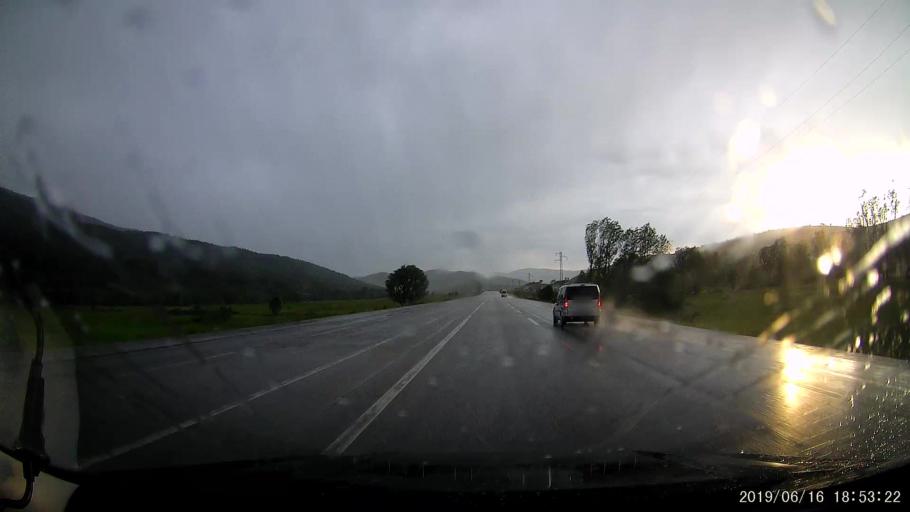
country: TR
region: Erzincan
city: Catalcam
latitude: 39.8987
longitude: 38.8788
